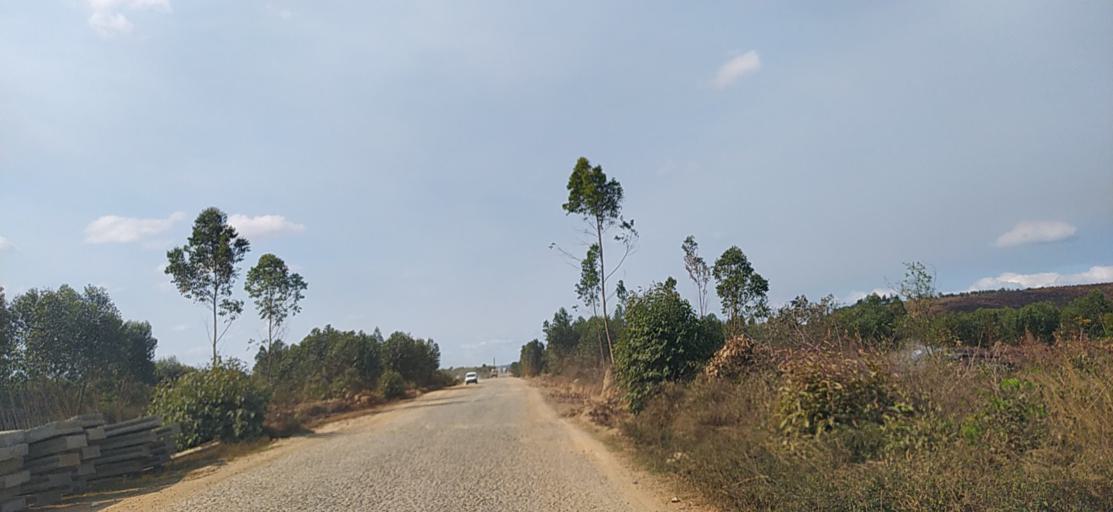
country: MG
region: Alaotra Mangoro
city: Moramanga
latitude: -18.6876
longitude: 48.2711
